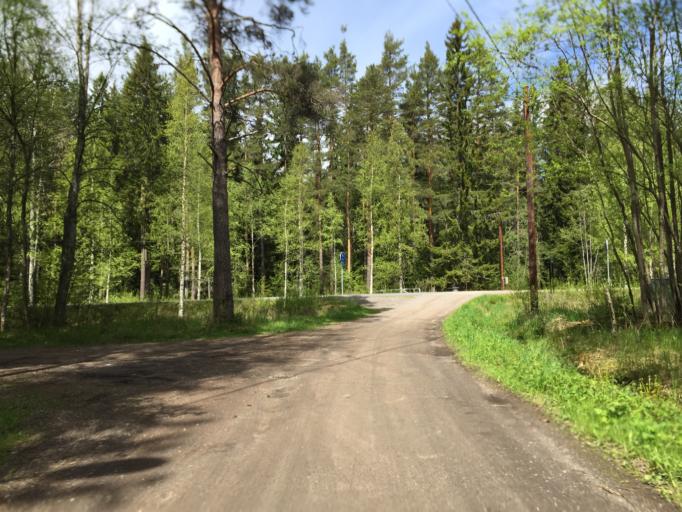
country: SE
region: Dalarna
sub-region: Ludvika Kommun
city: Ludvika
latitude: 60.1449
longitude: 15.1511
